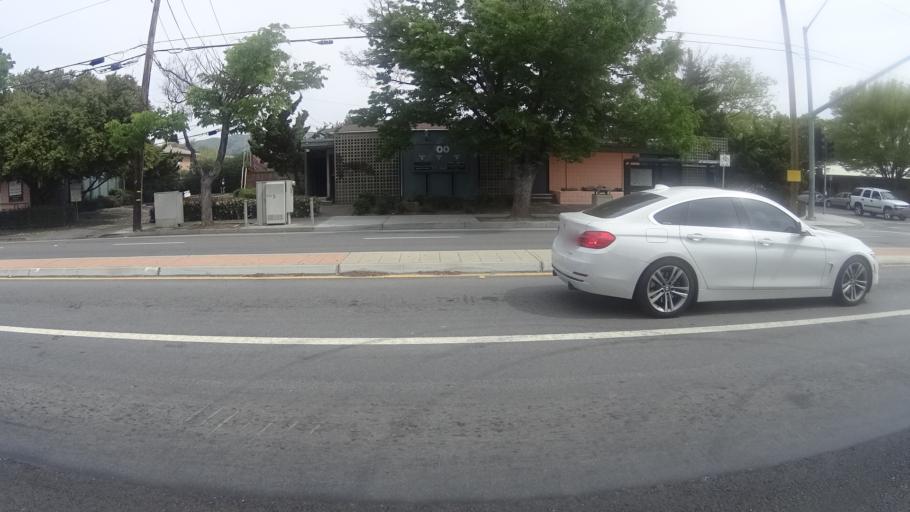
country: US
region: California
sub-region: Santa Clara County
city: Alum Rock
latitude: 37.3630
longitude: -121.8481
